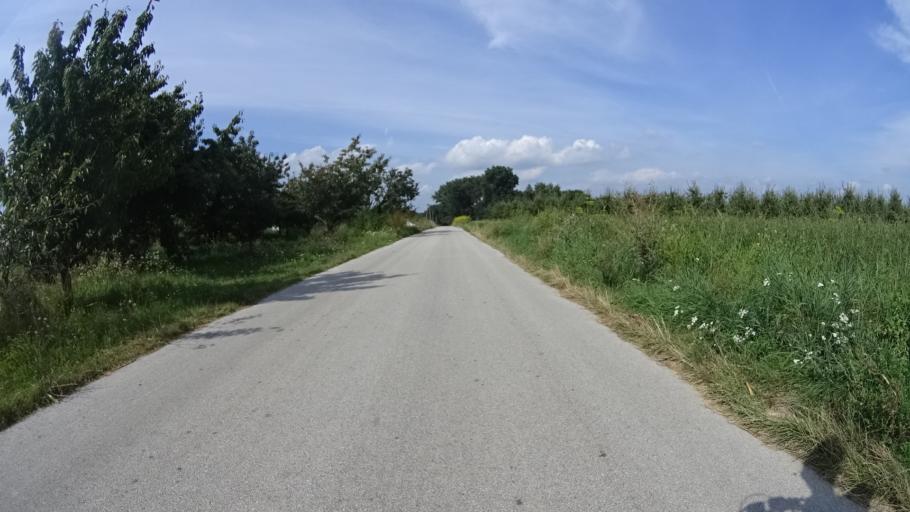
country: PL
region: Masovian Voivodeship
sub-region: Powiat grojecki
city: Goszczyn
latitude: 51.6963
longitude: 20.8476
